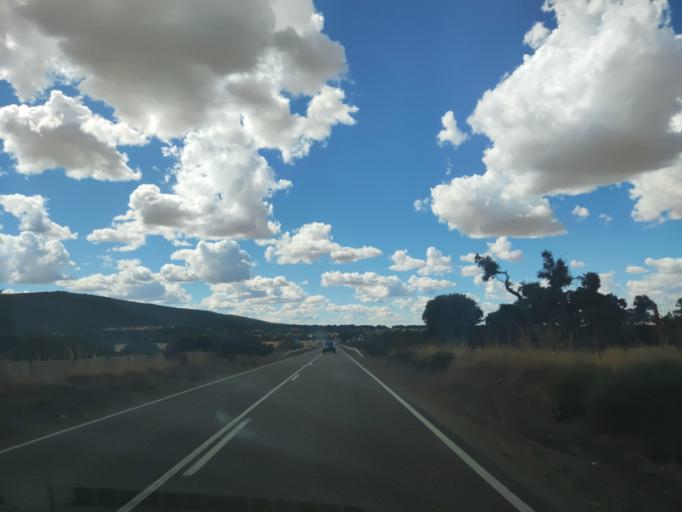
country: ES
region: Castille and Leon
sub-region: Provincia de Salamanca
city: Tejeda y Segoyuela
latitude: 40.6407
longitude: -6.0570
